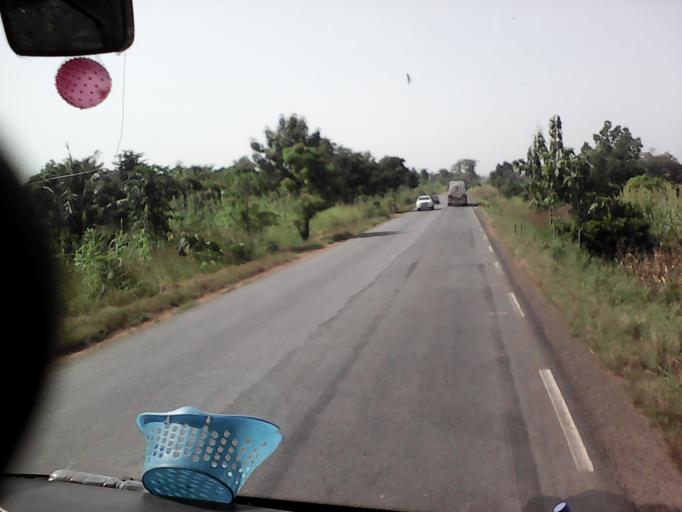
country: TG
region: Centrale
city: Sokode
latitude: 8.7863
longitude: 1.0671
